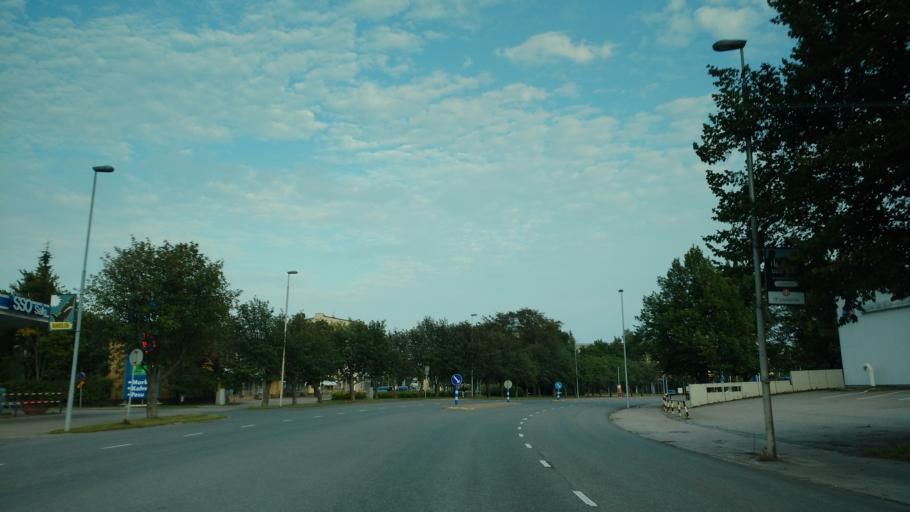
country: FI
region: Varsinais-Suomi
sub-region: Salo
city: Salo
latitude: 60.3911
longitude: 23.1154
